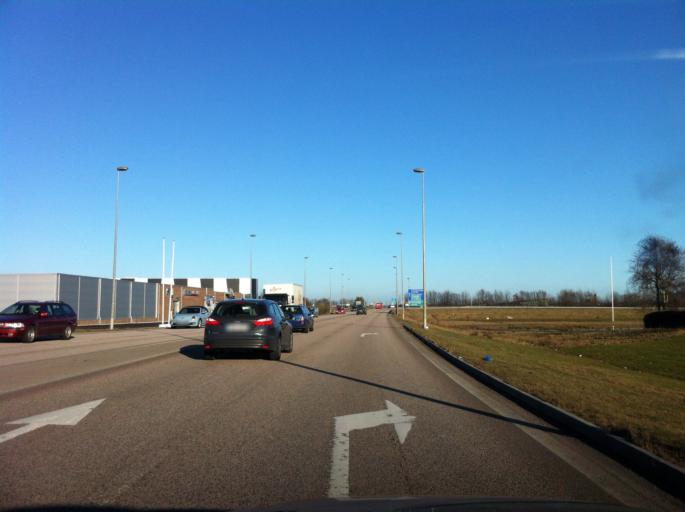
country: SE
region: Skane
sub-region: Angelholms Kommun
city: AEngelholm
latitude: 56.2513
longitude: 12.8937
